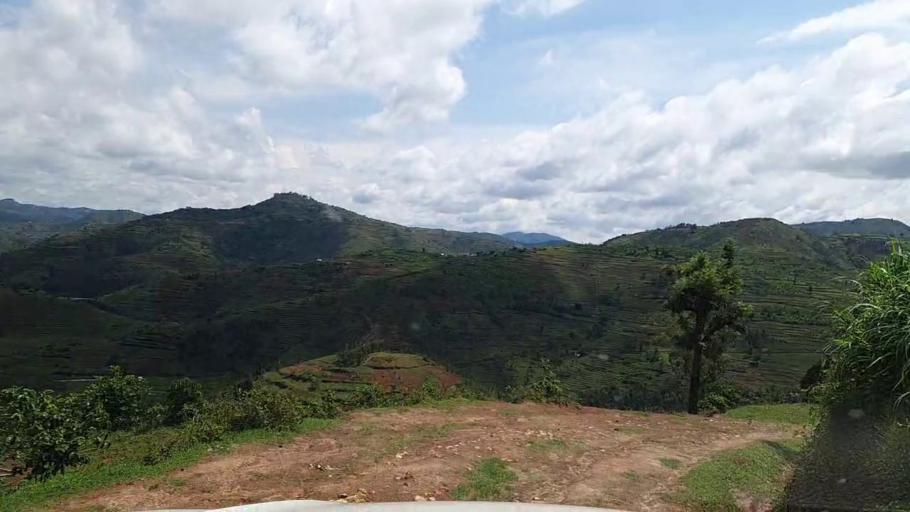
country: RW
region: Southern Province
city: Gikongoro
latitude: -2.3593
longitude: 29.5505
